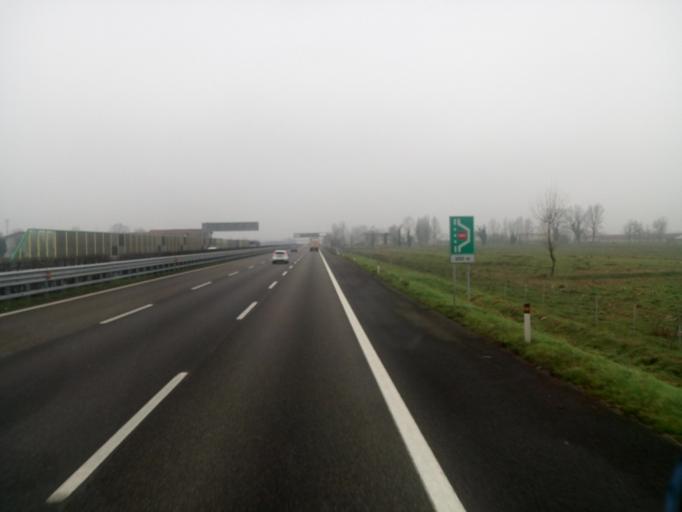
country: IT
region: Lombardy
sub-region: Provincia di Brescia
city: Bagnolo Mella
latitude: 45.4137
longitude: 10.1941
